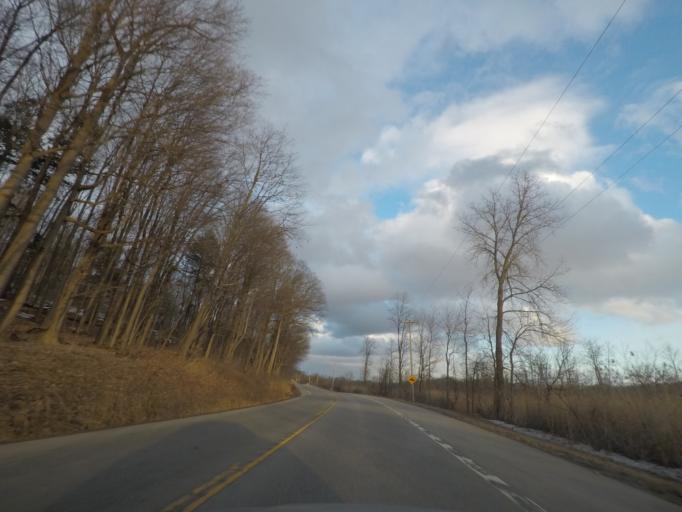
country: US
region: New York
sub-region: Montgomery County
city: Saint Johnsville
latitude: 43.0067
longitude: -74.7505
